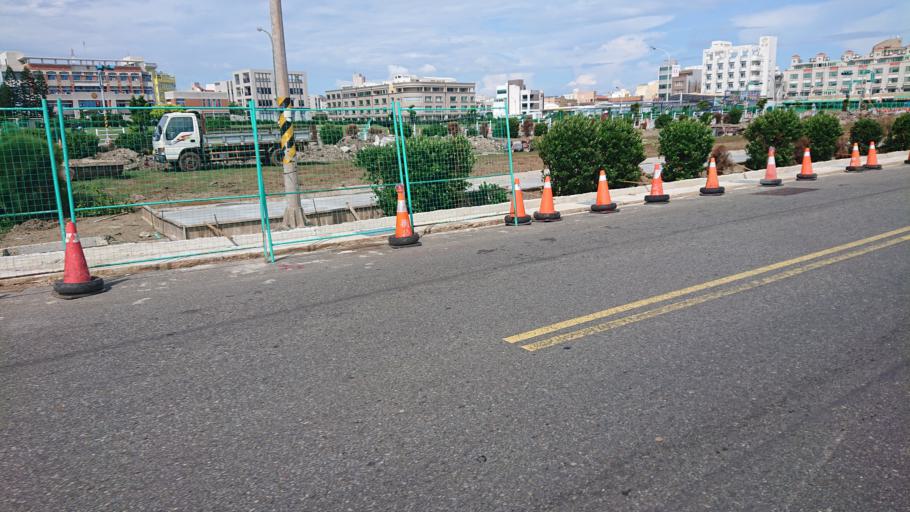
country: TW
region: Taiwan
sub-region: Penghu
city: Ma-kung
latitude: 23.5645
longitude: 119.5787
